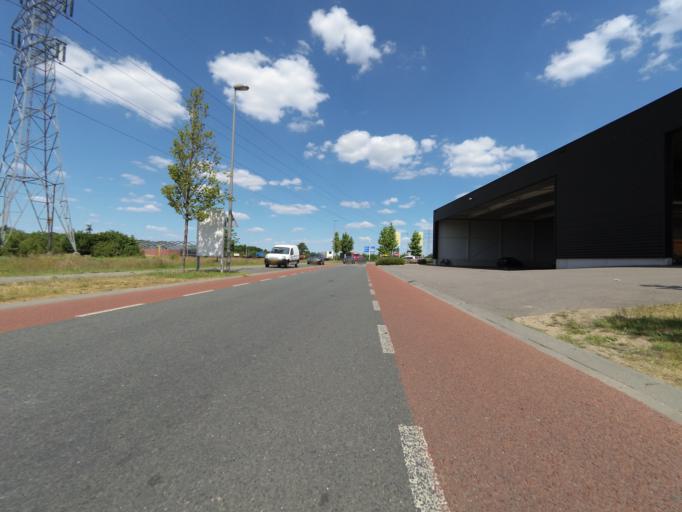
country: NL
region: Gelderland
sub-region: Gemeente Barneveld
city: Kootwijkerbroek
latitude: 52.1504
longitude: 5.6546
